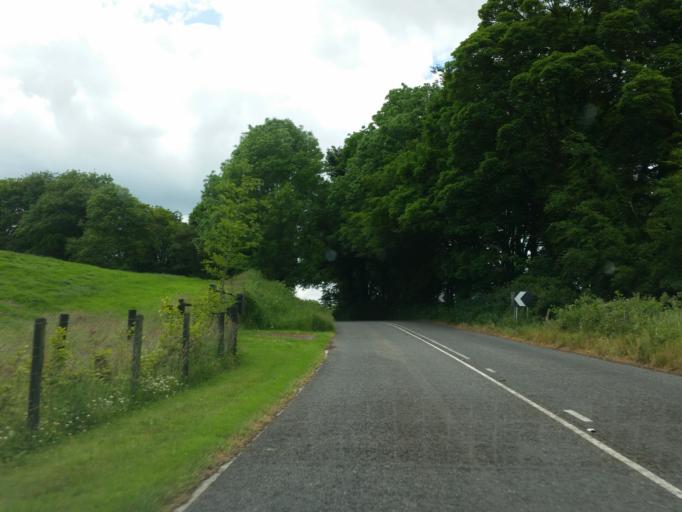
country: GB
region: Northern Ireland
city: Fivemiletown
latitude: 54.4465
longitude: -7.0836
